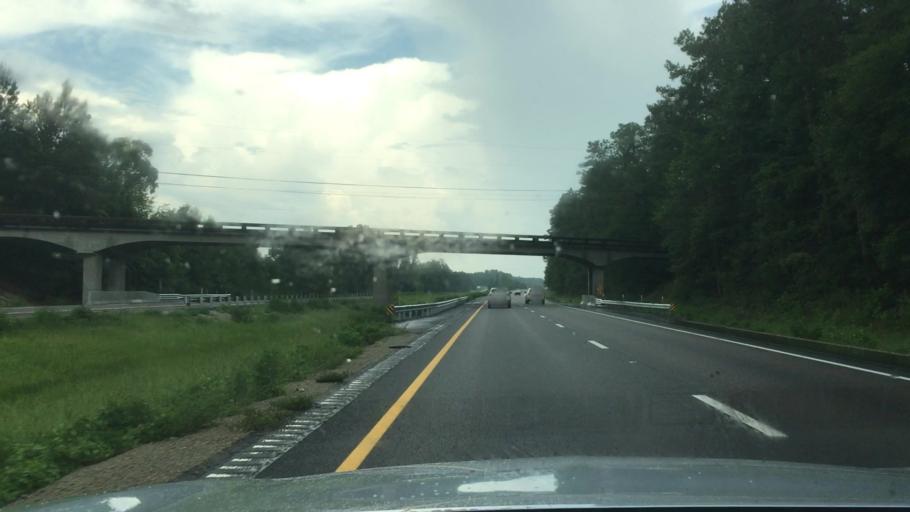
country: US
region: Mississippi
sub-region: Lamar County
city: Purvis
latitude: 31.1877
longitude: -89.3431
